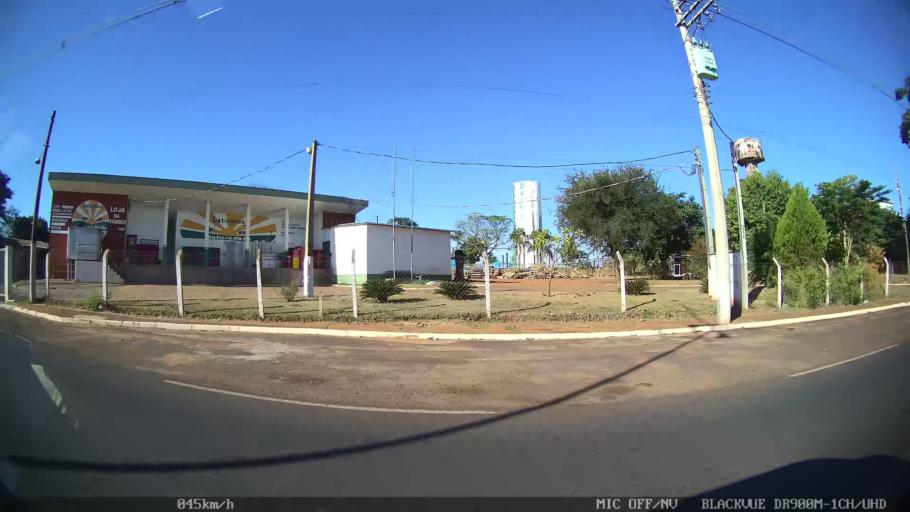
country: BR
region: Sao Paulo
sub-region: Olimpia
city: Olimpia
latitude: -20.7259
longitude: -48.9055
